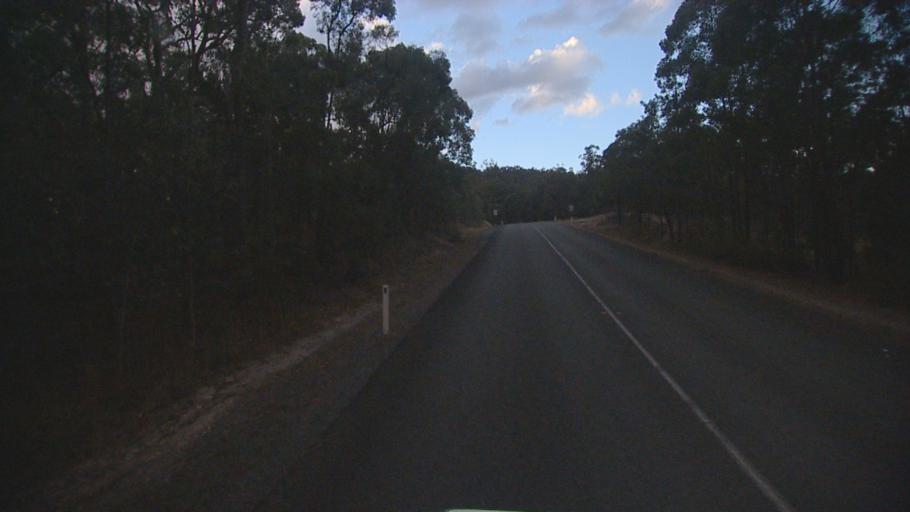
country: AU
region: Queensland
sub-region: Logan
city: Chambers Flat
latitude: -27.8029
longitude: 153.1438
